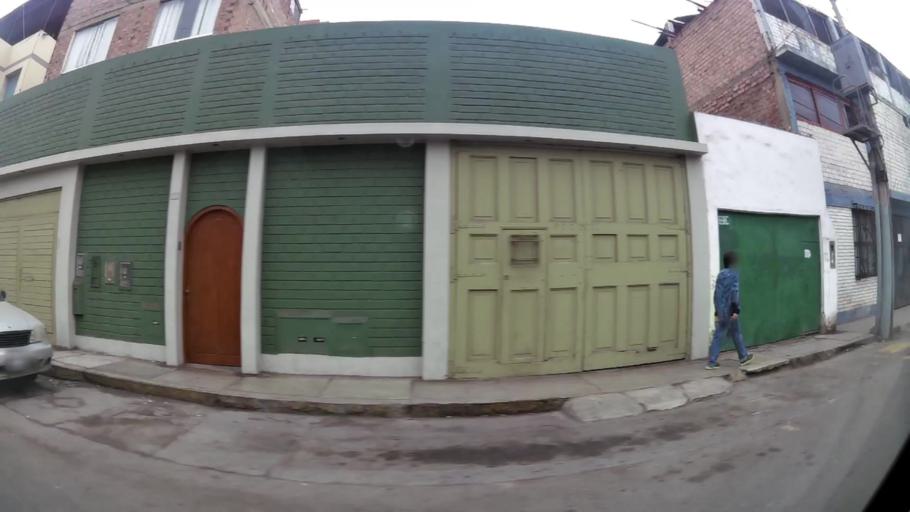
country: PE
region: Callao
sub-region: Callao
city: Callao
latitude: -12.0862
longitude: -77.0889
